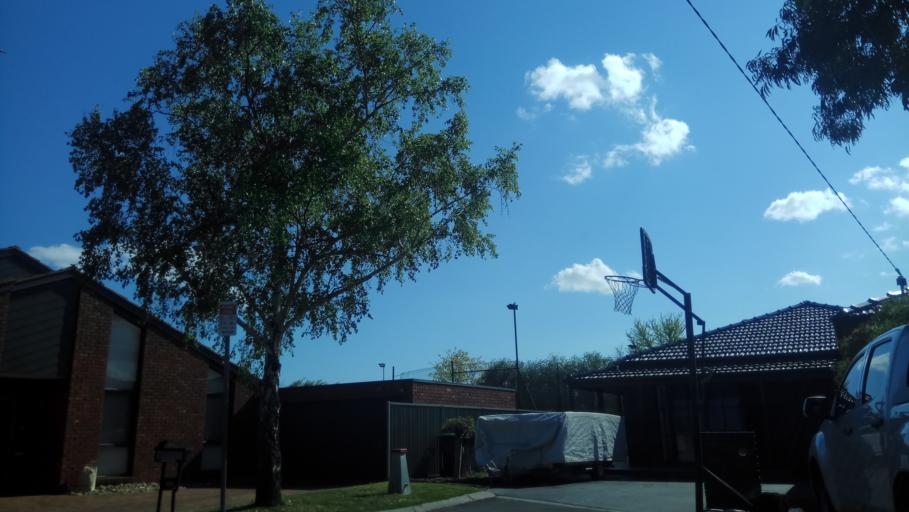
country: AU
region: Victoria
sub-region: Kingston
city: Dingley Village
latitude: -37.9831
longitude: 145.1251
